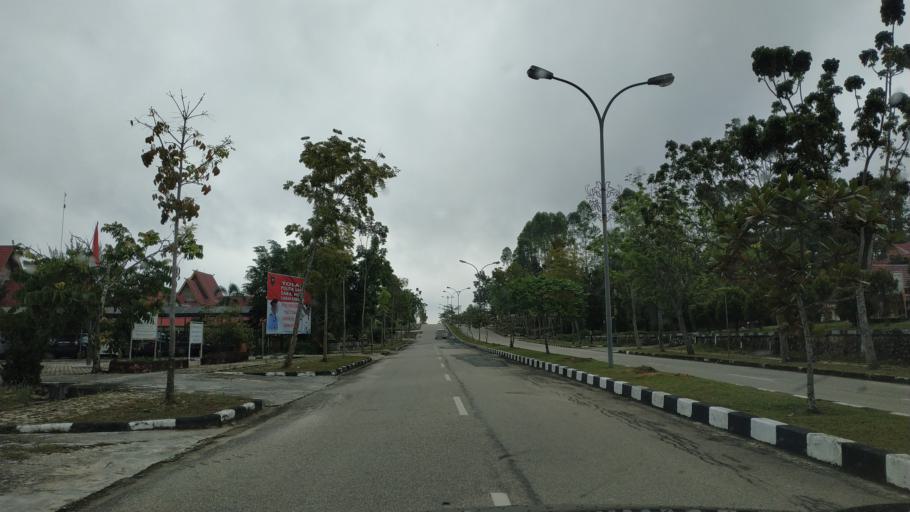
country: ID
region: Riau
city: Pangkalanbunut
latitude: 0.3808
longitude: 101.8249
